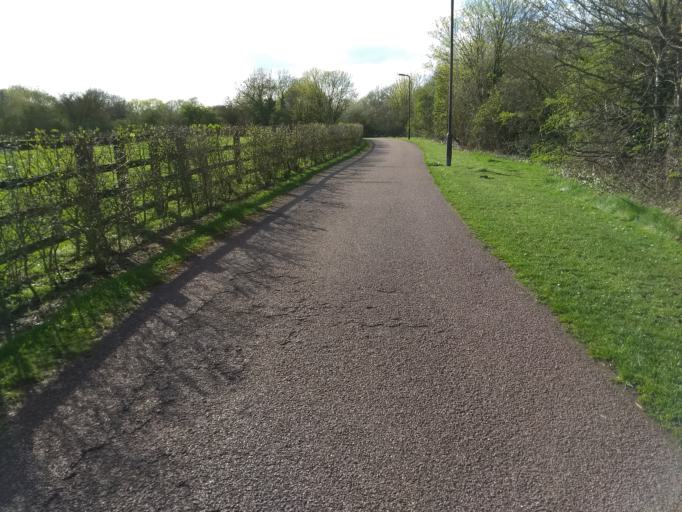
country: GB
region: England
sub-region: Milton Keynes
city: Simpson
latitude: 52.0239
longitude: -0.7178
